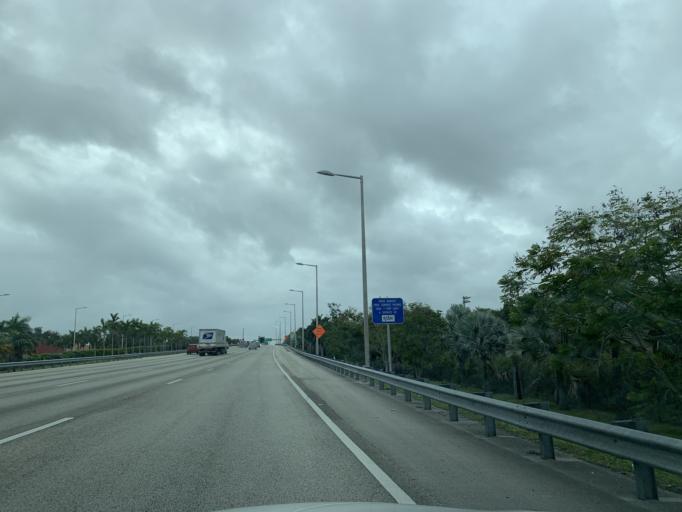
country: US
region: Florida
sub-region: Miami-Dade County
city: The Crossings
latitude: 25.6675
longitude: -80.3694
